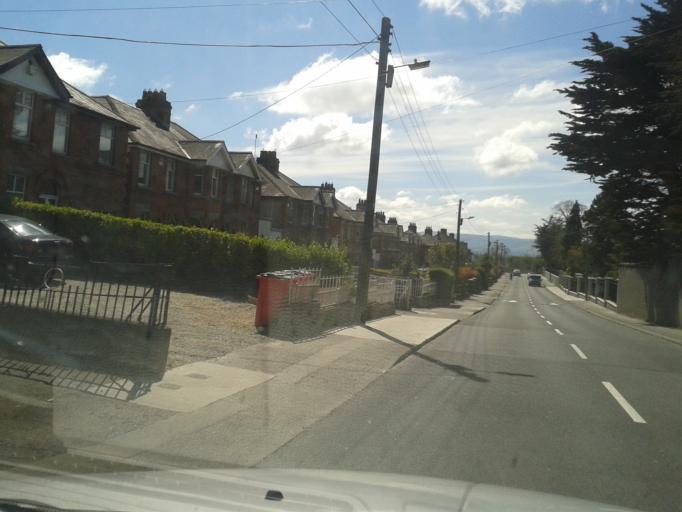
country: IE
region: Leinster
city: Marino
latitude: 53.3781
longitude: -6.2412
